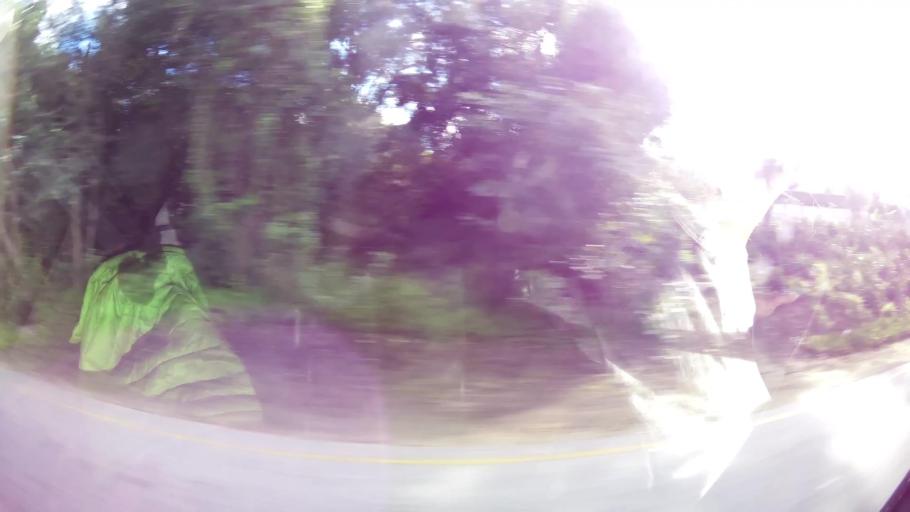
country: ZA
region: Western Cape
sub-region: Eden District Municipality
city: Knysna
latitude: -34.0379
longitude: 23.0638
